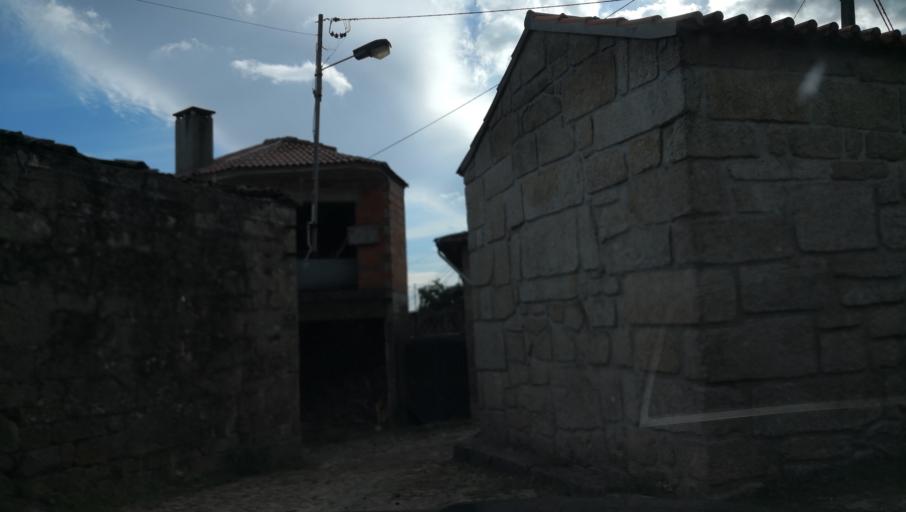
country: PT
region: Vila Real
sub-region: Vila Real
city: Vila Real
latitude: 41.3279
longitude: -7.7742
